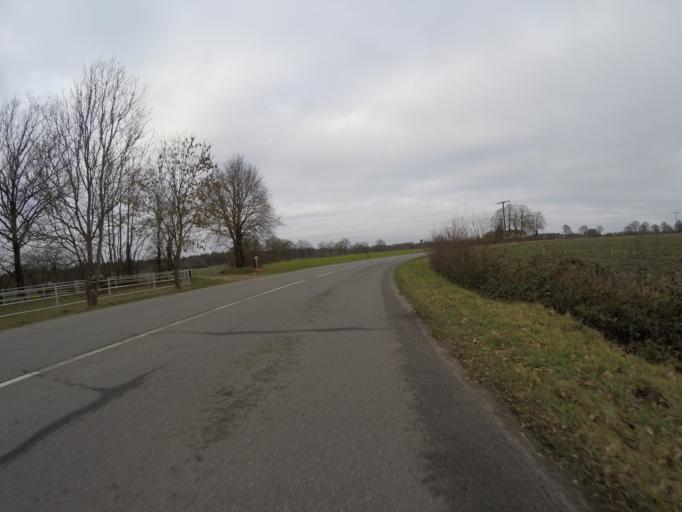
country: DE
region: Schleswig-Holstein
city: Langeln
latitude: 53.7877
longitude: 9.8358
